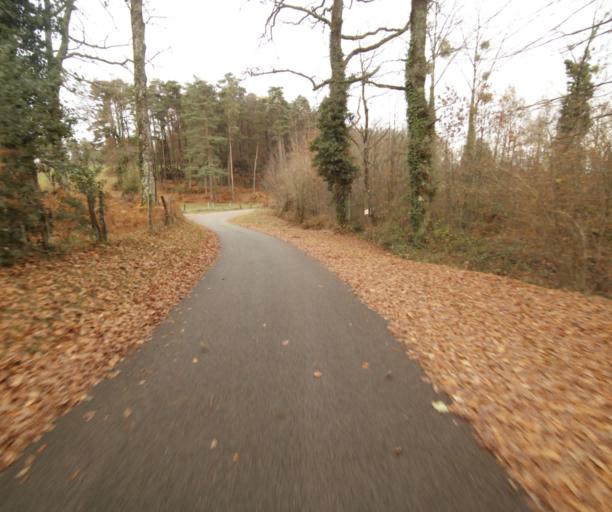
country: FR
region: Limousin
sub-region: Departement de la Correze
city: Saint-Mexant
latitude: 45.2573
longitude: 1.6642
